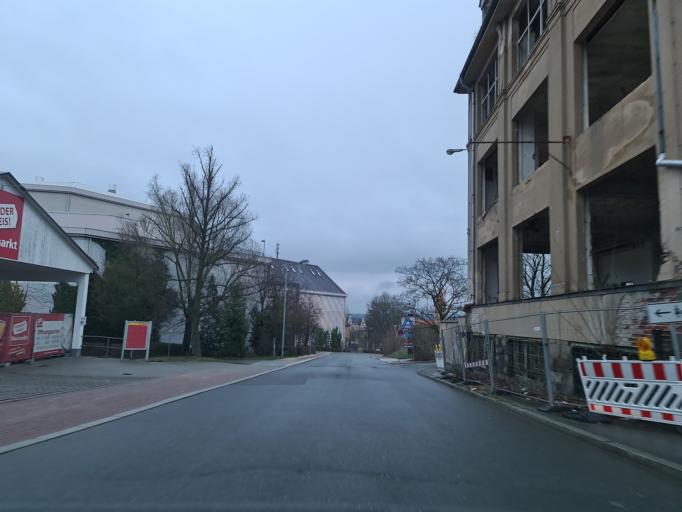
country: DE
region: Saxony
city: Plauen
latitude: 50.4953
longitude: 12.1002
